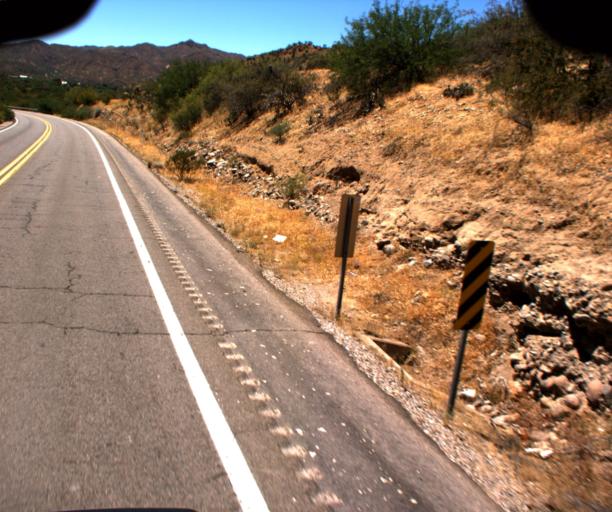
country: US
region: Arizona
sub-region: Pinal County
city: Kearny
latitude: 33.1252
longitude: -110.9782
